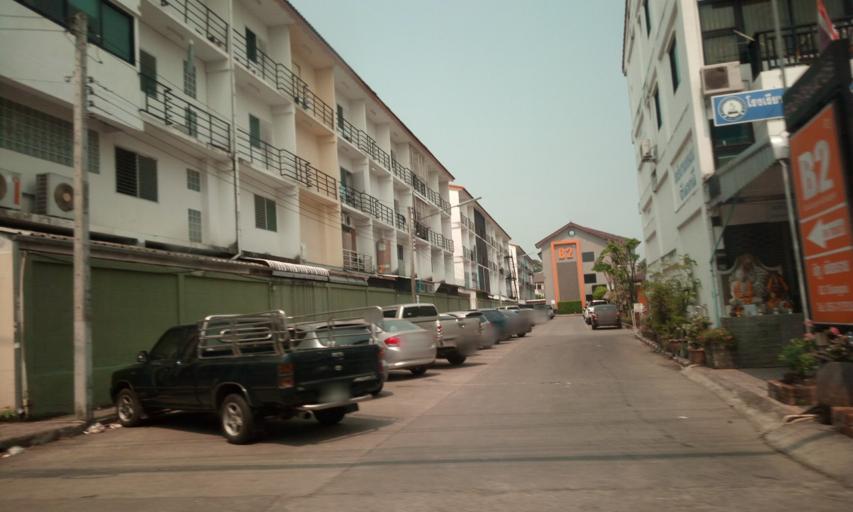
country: TH
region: Chiang Rai
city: Chiang Rai
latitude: 19.9073
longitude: 99.8266
